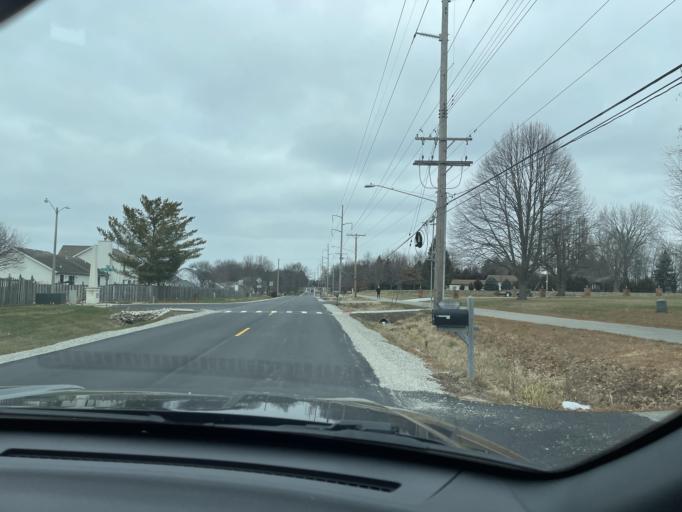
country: US
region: Illinois
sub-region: Sangamon County
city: Rochester
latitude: 39.7662
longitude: -89.5787
